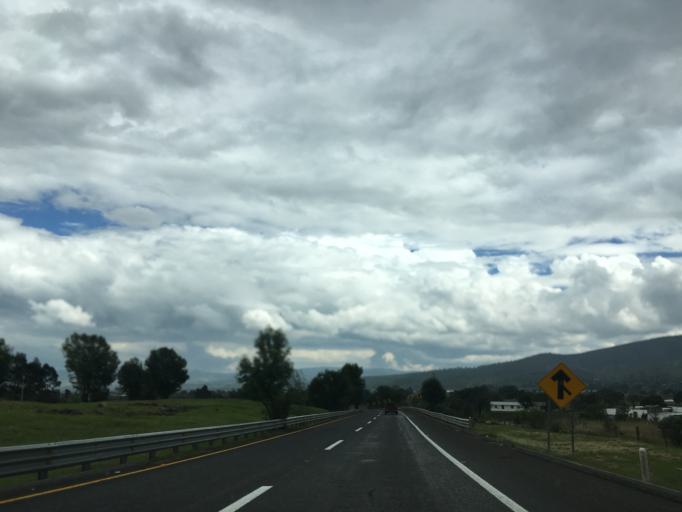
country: MX
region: Michoacan
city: Acuitzio del Canje
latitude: 19.5558
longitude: -101.3390
